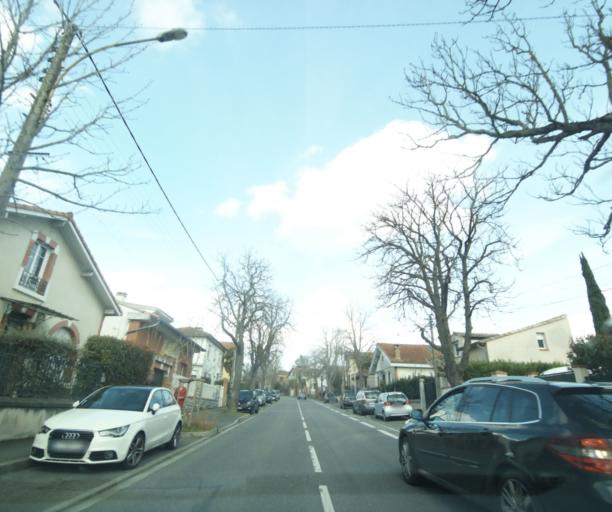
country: FR
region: Midi-Pyrenees
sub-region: Departement de la Haute-Garonne
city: Toulouse
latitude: 43.5923
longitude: 1.4713
